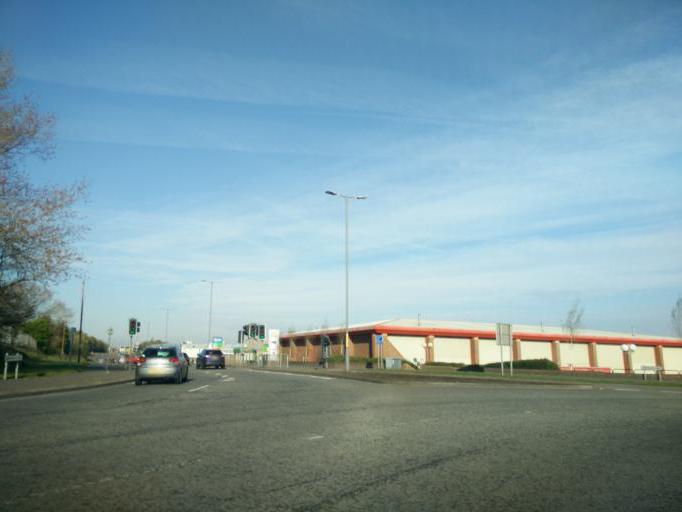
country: GB
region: England
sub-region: Stockton-on-Tees
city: Billingham
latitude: 54.5720
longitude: -1.2887
